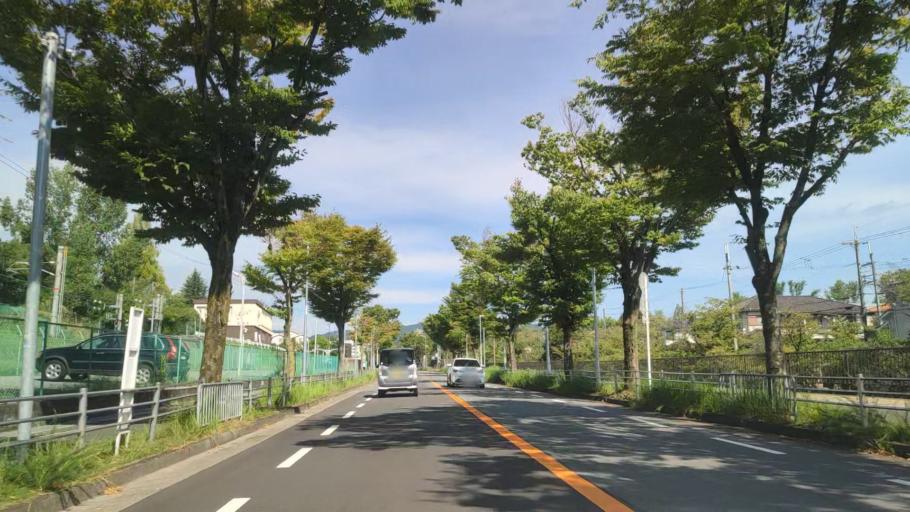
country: JP
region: Osaka
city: Mino
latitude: 34.8221
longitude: 135.5103
